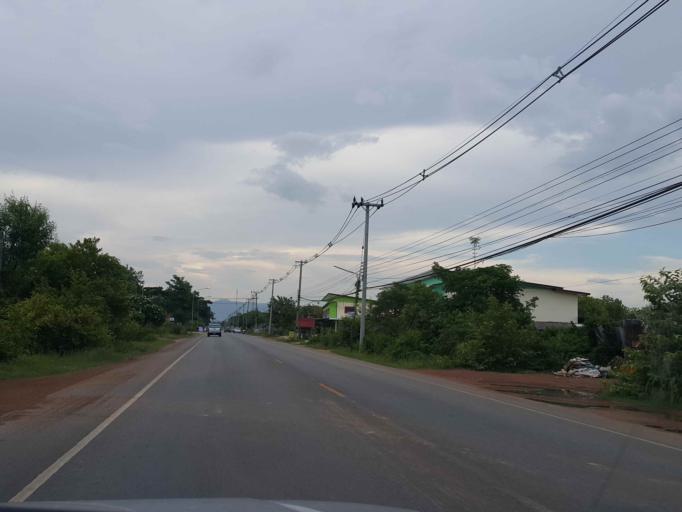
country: TH
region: Lampang
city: Hang Chat
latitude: 18.2710
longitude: 99.3867
